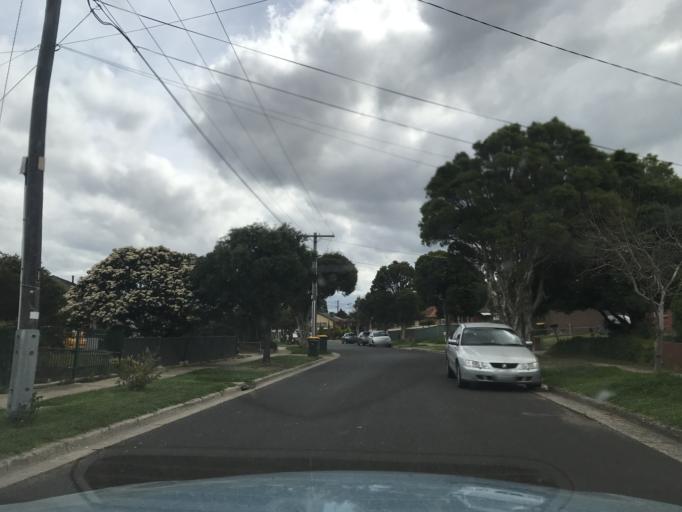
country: AU
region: Victoria
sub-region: Hobsons Bay
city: Laverton
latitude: -37.8475
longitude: 144.7775
